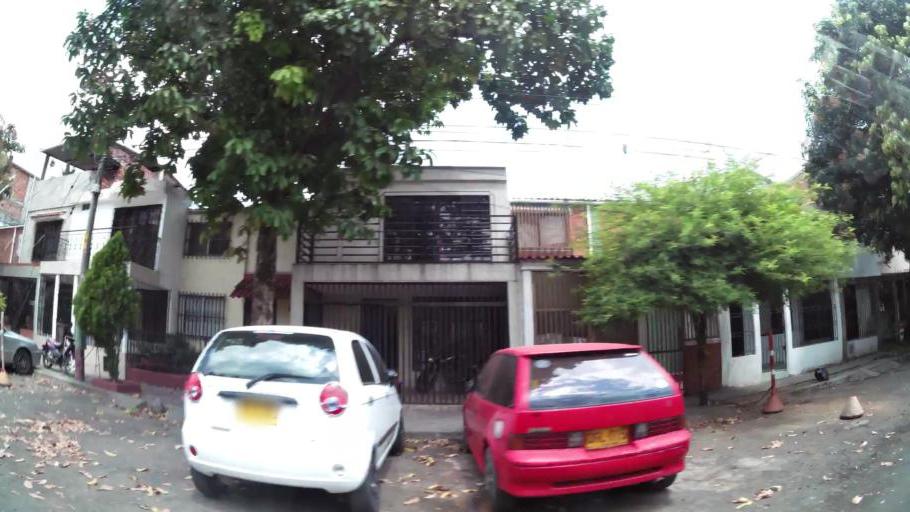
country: CO
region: Valle del Cauca
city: Cali
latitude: 3.4675
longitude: -76.4933
